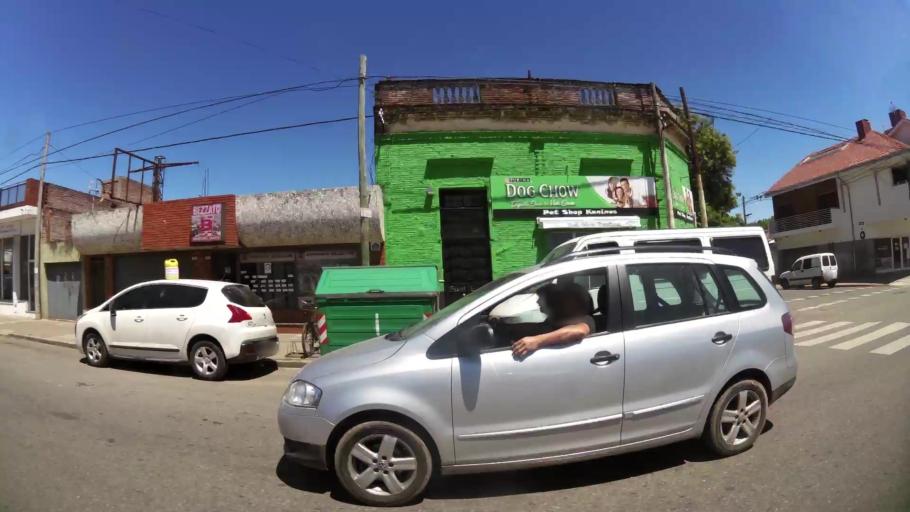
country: AR
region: Santa Fe
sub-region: Departamento de Rosario
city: Rosario
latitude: -32.9426
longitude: -60.7125
